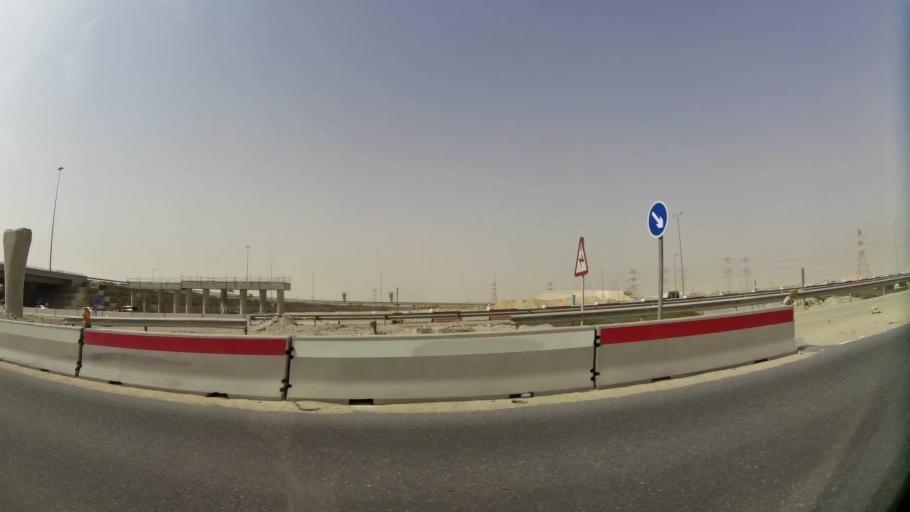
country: QA
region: Baladiyat ar Rayyan
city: Ar Rayyan
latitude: 25.1729
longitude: 51.3290
